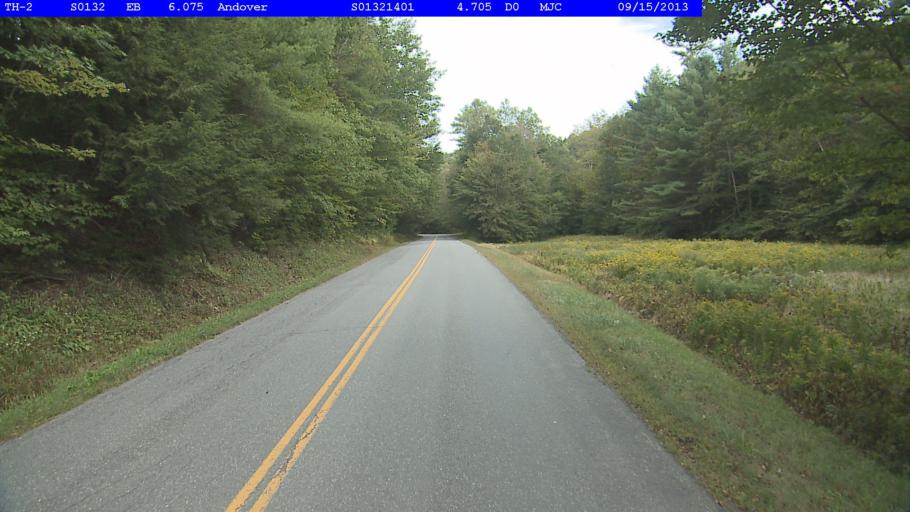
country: US
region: Vermont
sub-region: Windsor County
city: Chester
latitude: 43.2719
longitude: -72.6862
